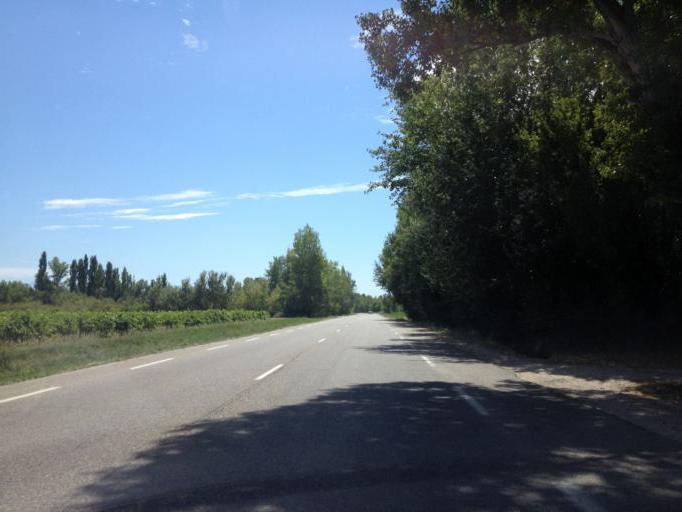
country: FR
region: Provence-Alpes-Cote d'Azur
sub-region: Departement du Vaucluse
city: Bedarrides
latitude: 44.0293
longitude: 4.8831
